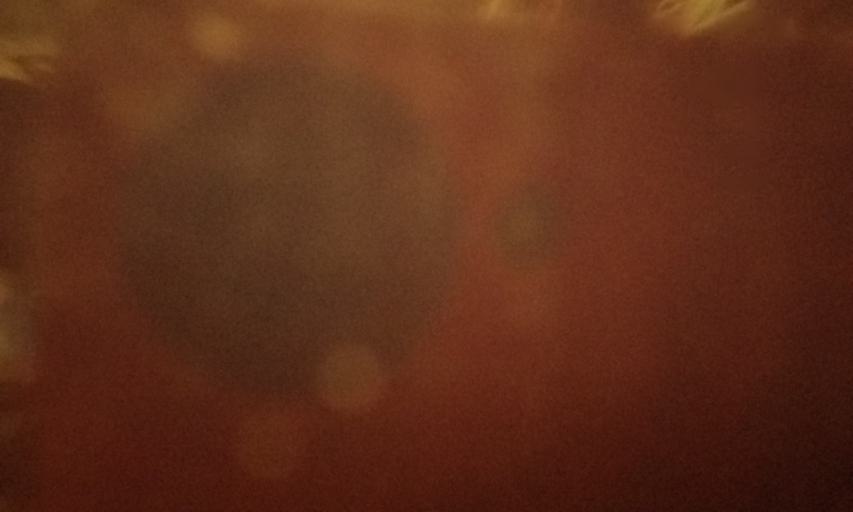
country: JP
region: Hyogo
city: Ashiya
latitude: 34.7407
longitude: 135.2885
